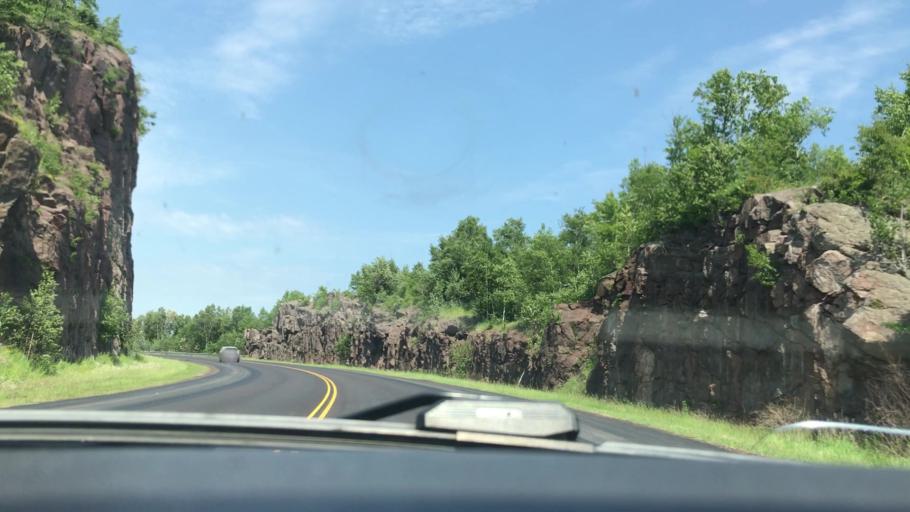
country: US
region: Minnesota
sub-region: Lake County
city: Silver Bay
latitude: 47.3688
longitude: -91.1673
